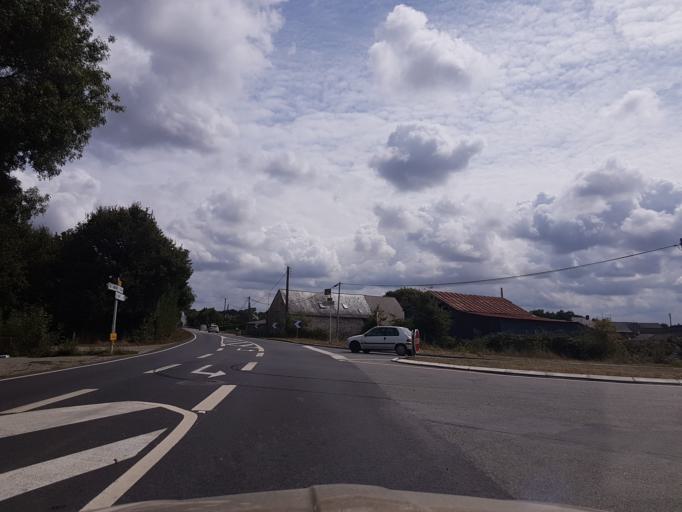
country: FR
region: Pays de la Loire
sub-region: Departement de la Loire-Atlantique
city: Ligne
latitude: 47.4149
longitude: -1.4091
